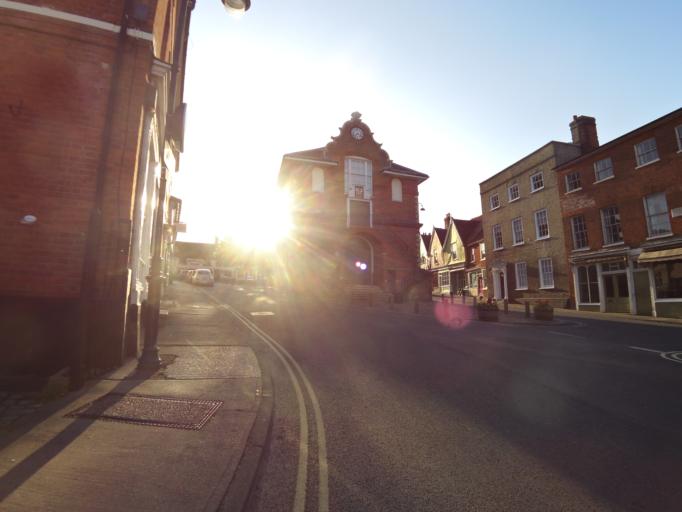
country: GB
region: England
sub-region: Suffolk
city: Woodbridge
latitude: 52.0939
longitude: 1.3141
